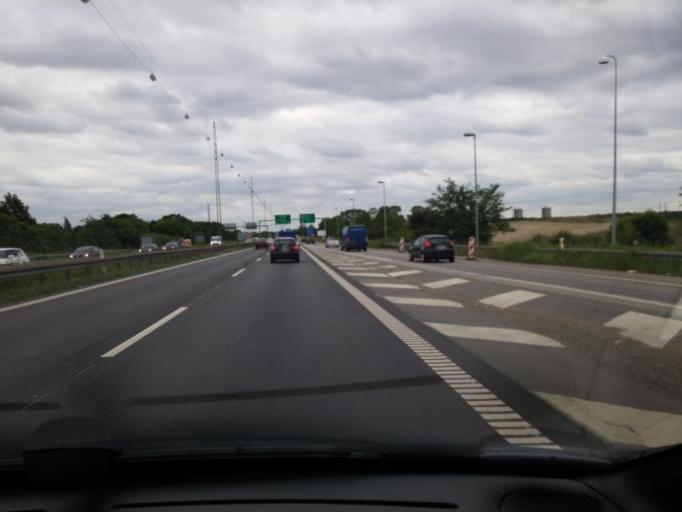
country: DK
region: Capital Region
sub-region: Brondby Kommune
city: Brondbyvester
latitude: 55.6389
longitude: 12.4257
